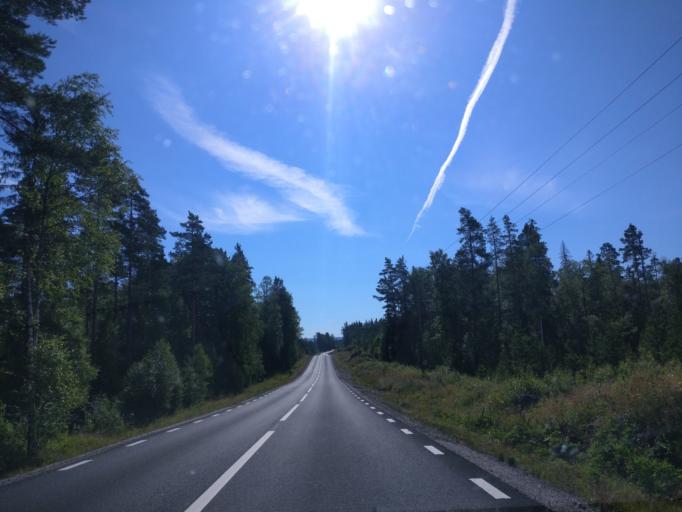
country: SE
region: Vaermland
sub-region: Hagfors Kommun
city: Hagfors
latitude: 60.0471
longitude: 13.8015
